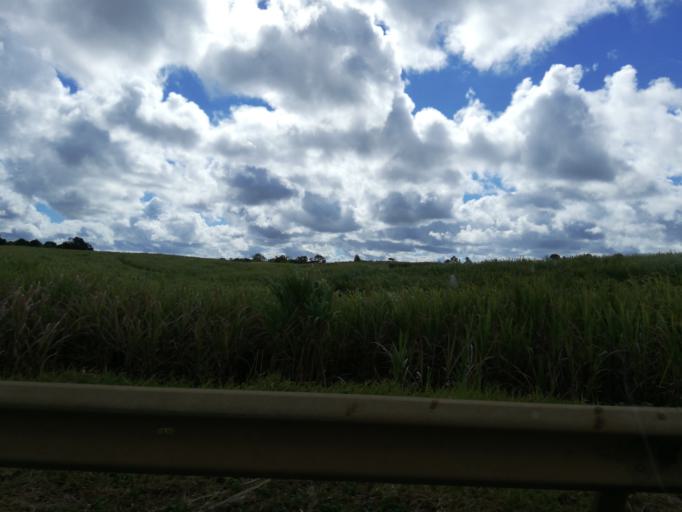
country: MU
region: Grand Port
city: Plaine Magnien
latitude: -20.4219
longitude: 57.6608
